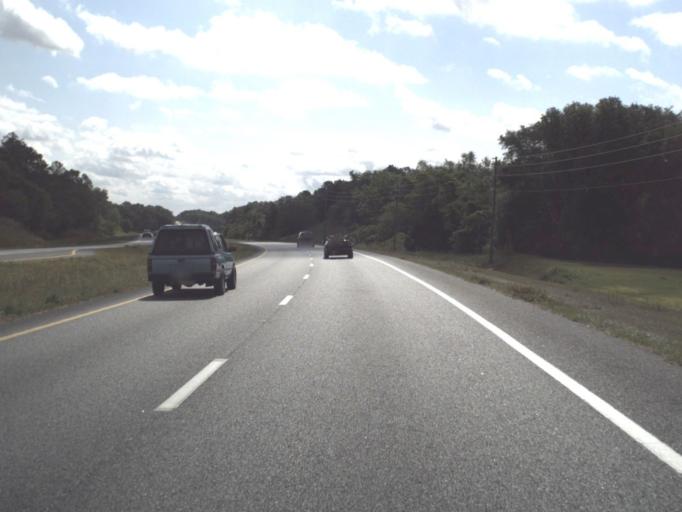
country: US
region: Florida
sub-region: Marion County
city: Ocala
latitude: 29.2601
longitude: -82.1648
